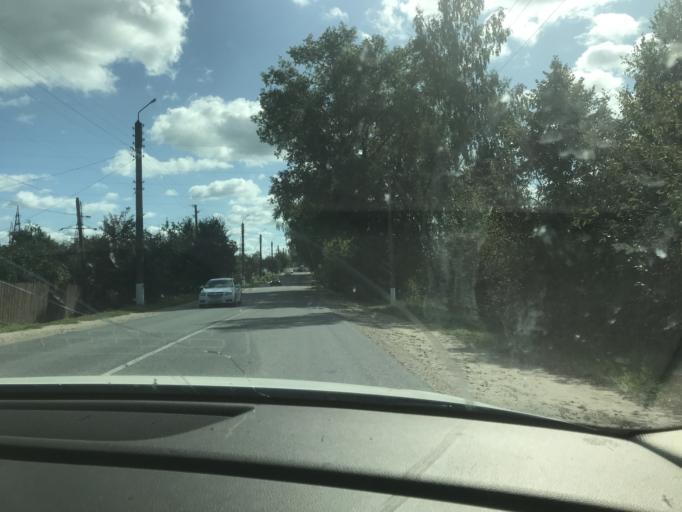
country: RU
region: Kaluga
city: Kondrovo
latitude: 54.8040
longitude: 35.9466
